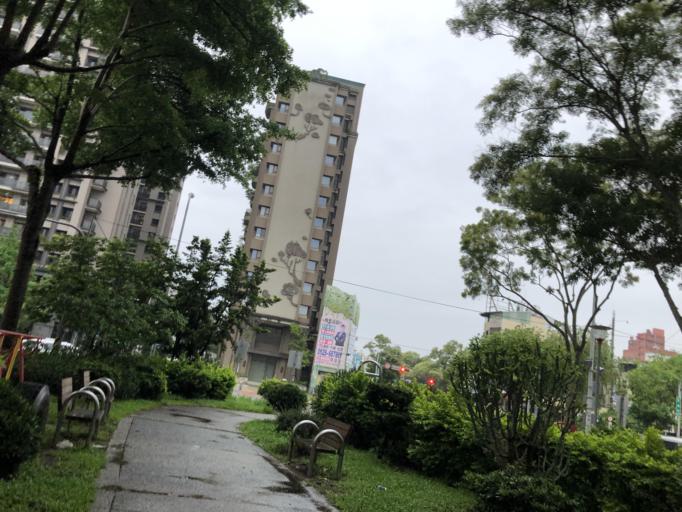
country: TW
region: Taiwan
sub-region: Taichung City
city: Taichung
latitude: 24.1568
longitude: 120.6756
